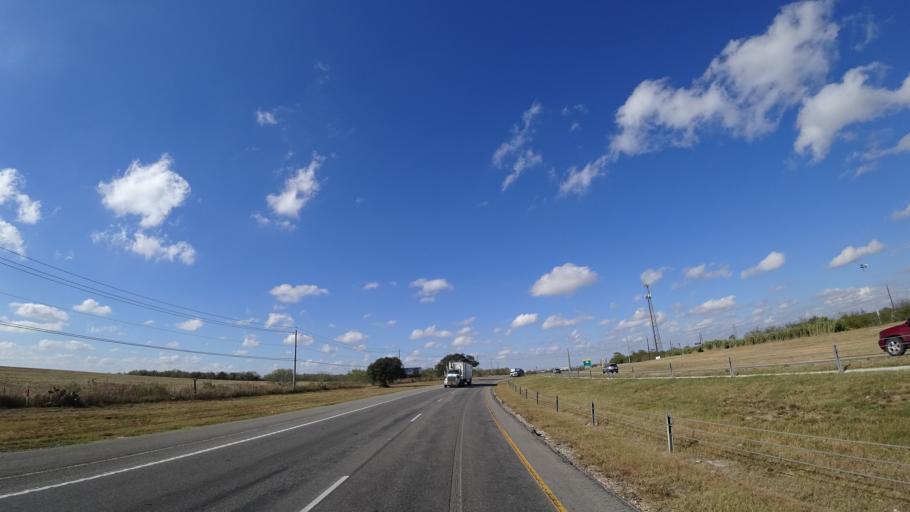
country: US
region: Texas
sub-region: Travis County
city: Garfield
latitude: 30.1860
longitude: -97.6132
